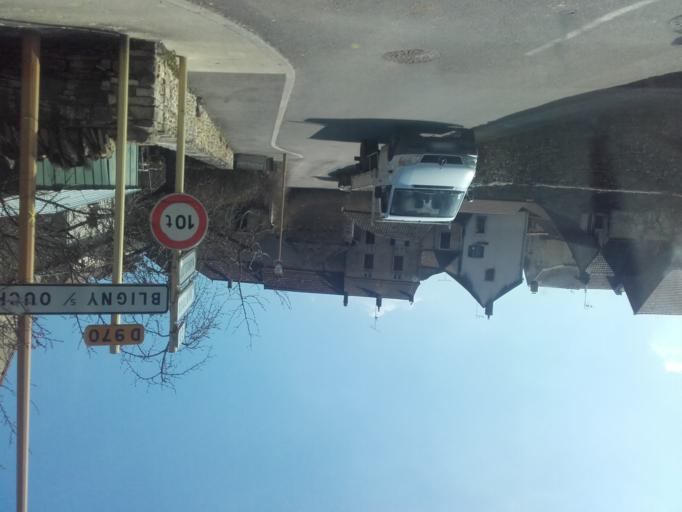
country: FR
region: Bourgogne
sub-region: Departement de la Cote-d'Or
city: Savigny-les-Beaune
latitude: 47.0521
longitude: 4.7707
